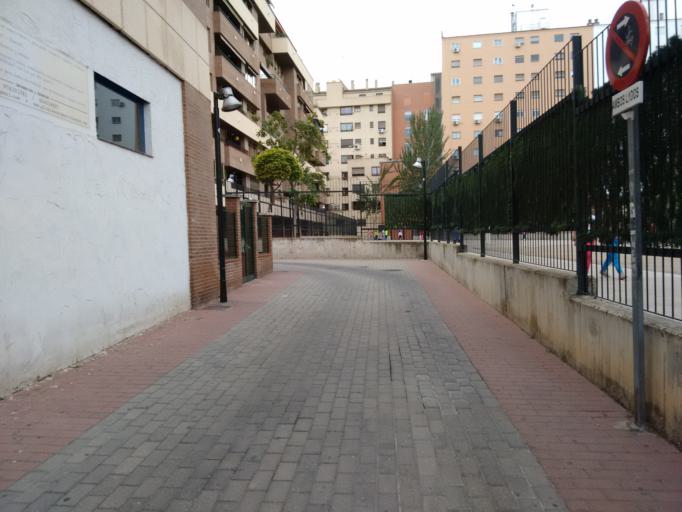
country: ES
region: Aragon
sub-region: Provincia de Zaragoza
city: Zaragoza
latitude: 41.6395
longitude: -0.8781
